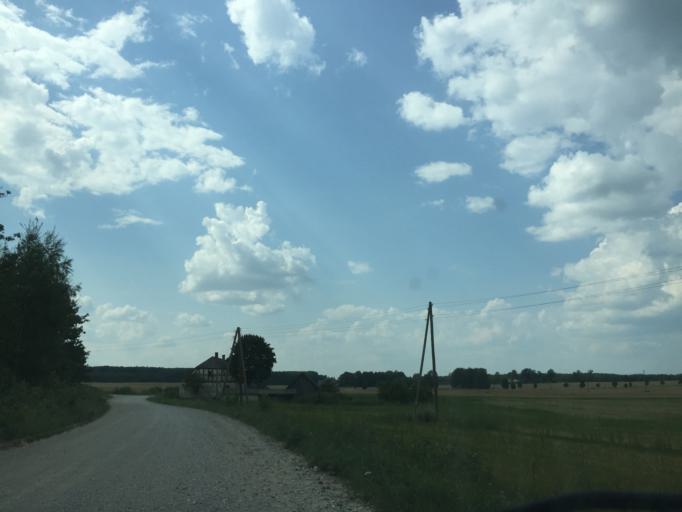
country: LV
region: Auces Novads
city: Auce
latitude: 56.4057
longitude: 23.0439
